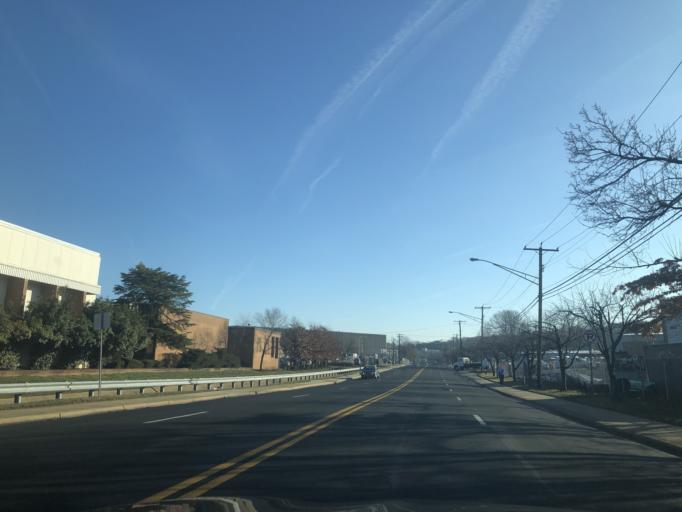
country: US
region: Maryland
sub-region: Prince George's County
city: Landover Hills
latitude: 38.9358
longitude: -76.8823
